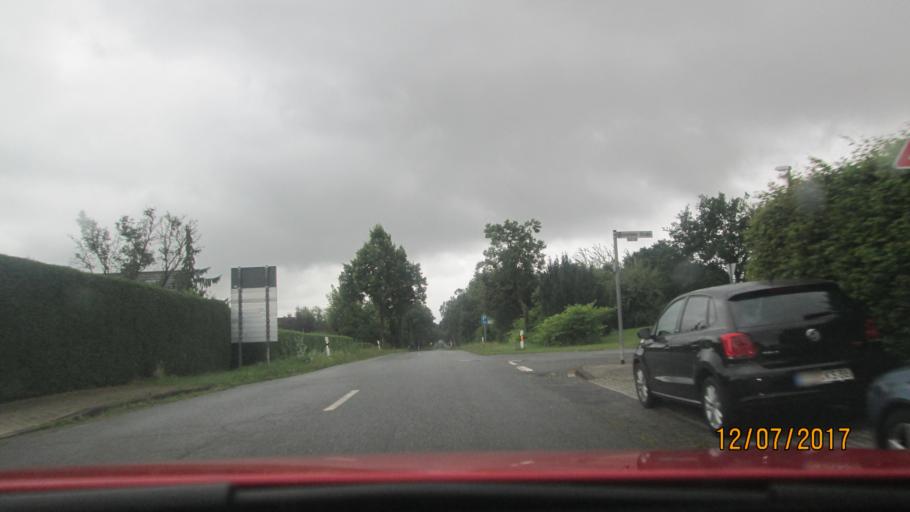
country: DE
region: Lower Saxony
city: Weyhausen
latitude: 52.3979
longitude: 10.6922
